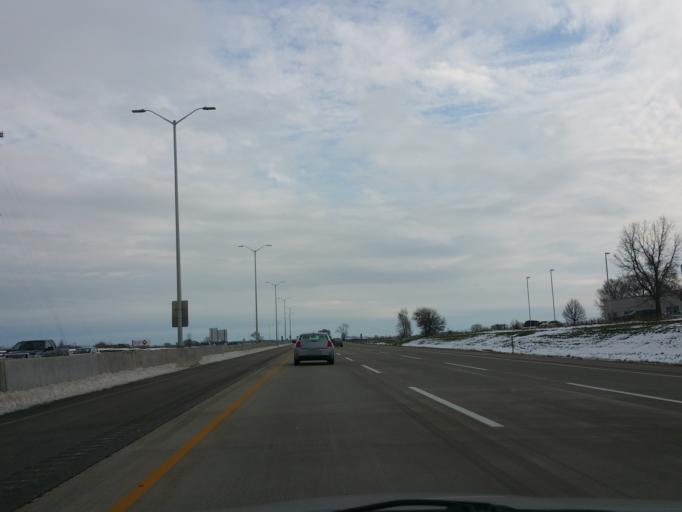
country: US
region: Illinois
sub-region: Winnebago County
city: Cherry Valley
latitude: 42.2389
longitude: -88.9166
